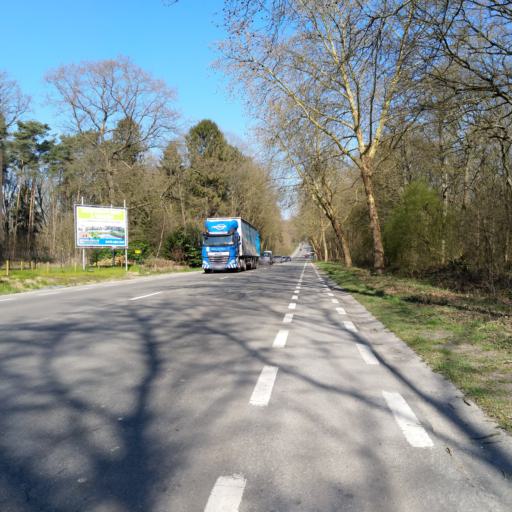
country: BE
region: Wallonia
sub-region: Province du Hainaut
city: Mons
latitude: 50.4929
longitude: 3.9397
